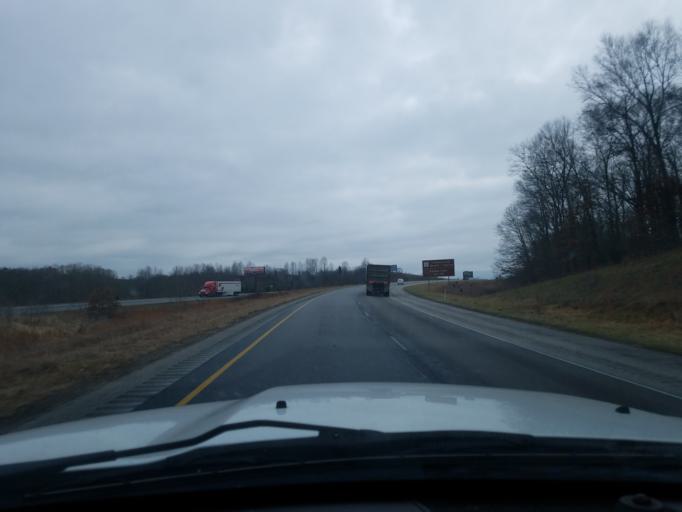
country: US
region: Indiana
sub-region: Crawford County
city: English
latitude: 38.2299
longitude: -86.5692
